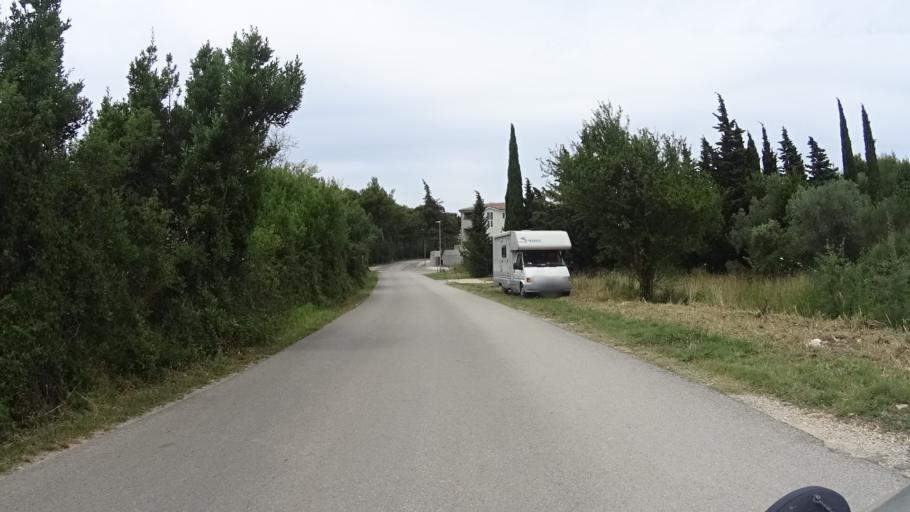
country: HR
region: Istarska
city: Medulin
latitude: 44.8009
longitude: 13.9063
